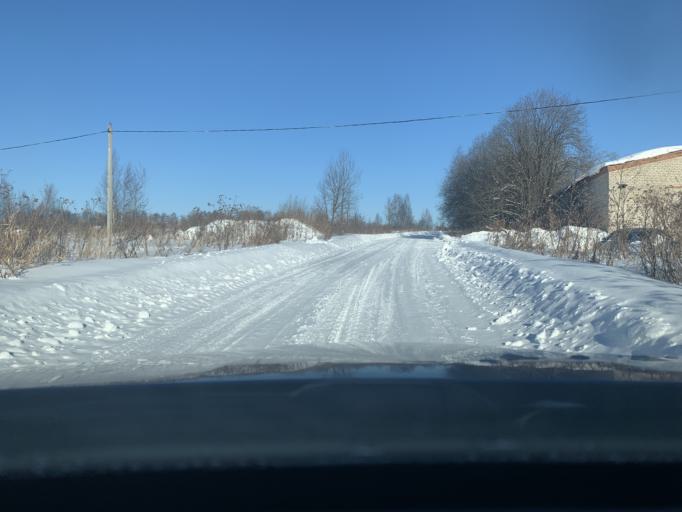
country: RU
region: Jaroslavl
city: Tunoshna
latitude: 57.6543
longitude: 40.0677
